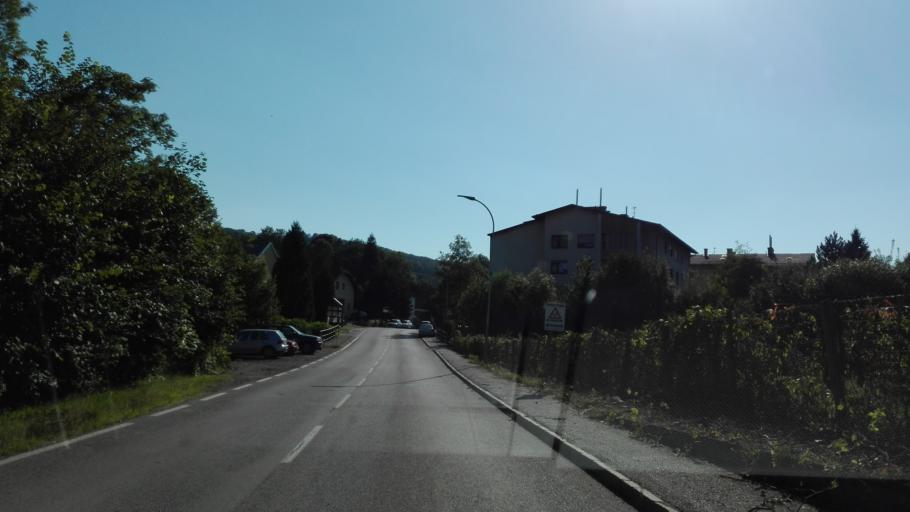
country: AT
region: Lower Austria
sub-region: Politischer Bezirk Sankt Polten
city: Altlengbach
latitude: 48.1538
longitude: 15.9442
